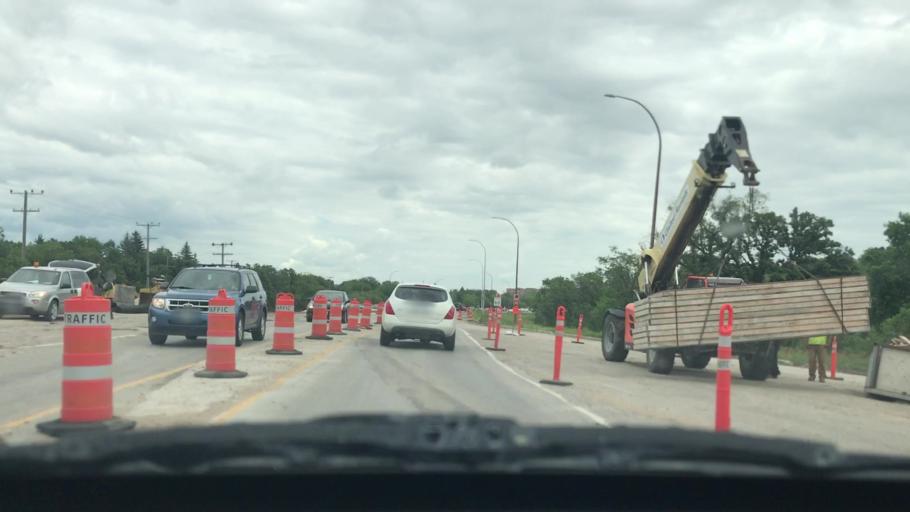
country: CA
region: Manitoba
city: Winnipeg
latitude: 49.8579
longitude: -97.0977
